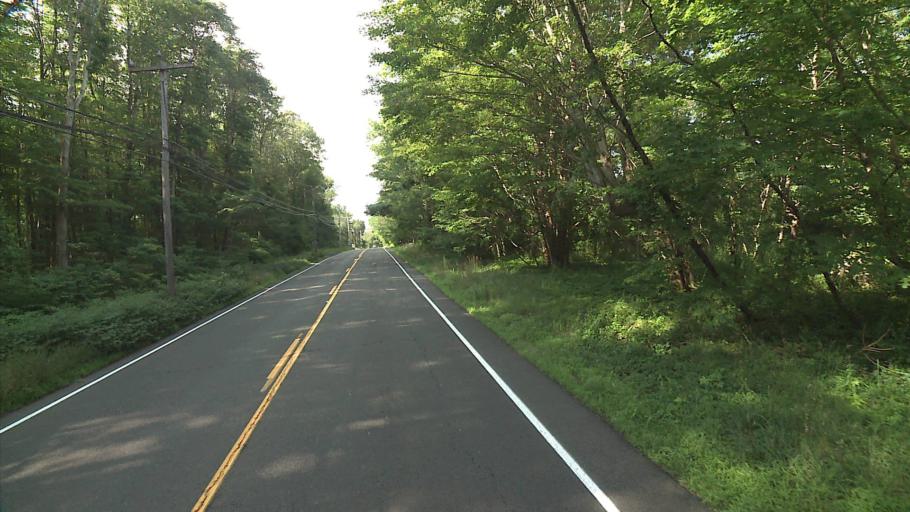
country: US
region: Connecticut
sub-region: Middlesex County
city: Higganum
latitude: 41.4229
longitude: -72.5624
